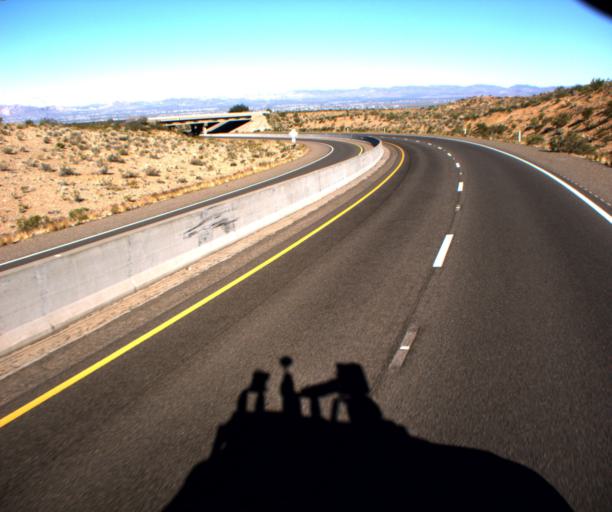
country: US
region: Arizona
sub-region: Mohave County
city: Kingman
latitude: 35.2218
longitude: -114.1227
